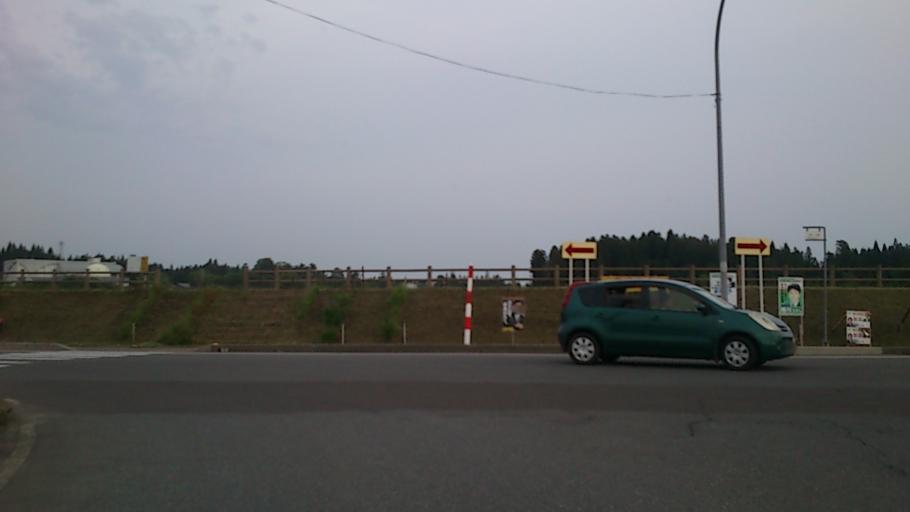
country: JP
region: Akita
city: Noshiromachi
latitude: 40.0907
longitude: 140.0841
